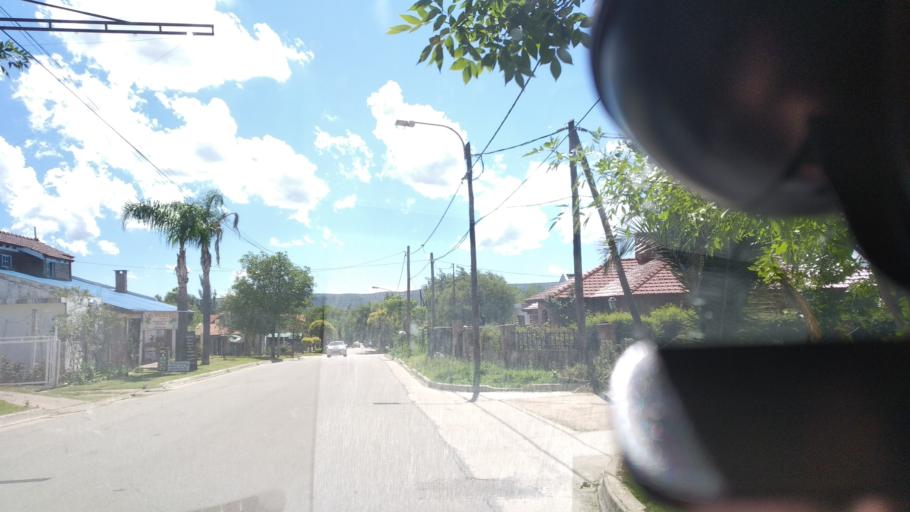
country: AR
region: Cordoba
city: Mina Clavero
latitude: -31.7240
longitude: -65.0087
